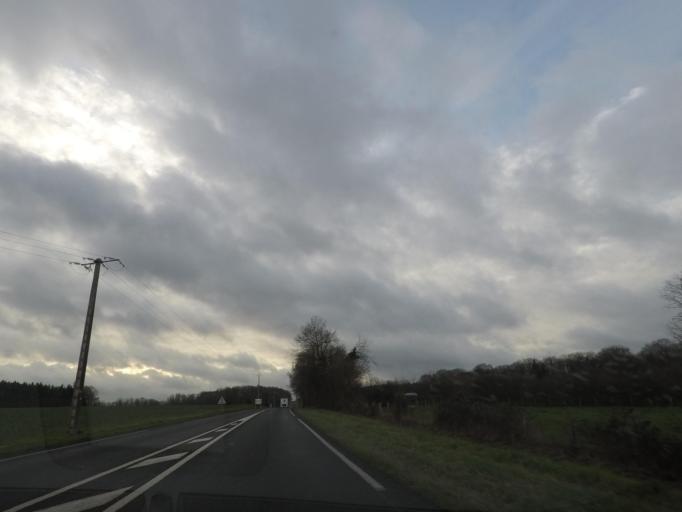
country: FR
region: Pays de la Loire
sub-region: Departement de la Sarthe
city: Vibraye
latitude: 48.1026
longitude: 0.7180
